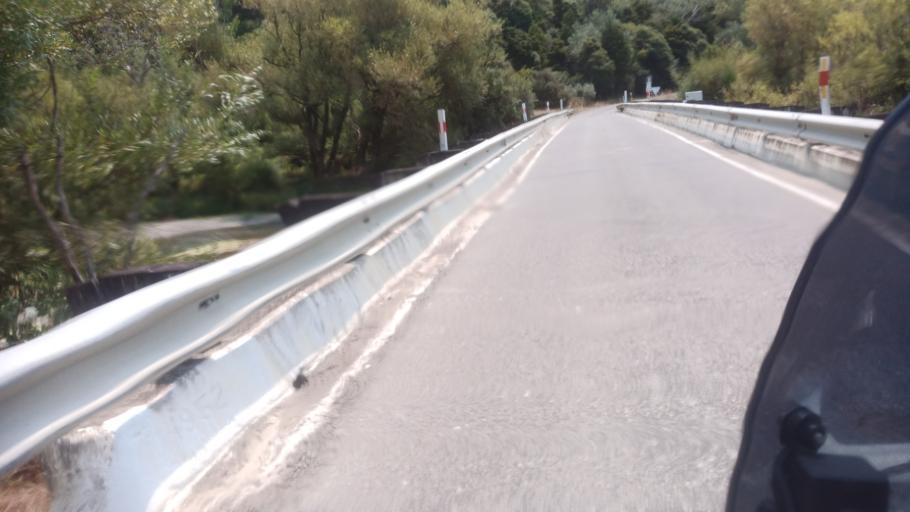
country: NZ
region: Bay of Plenty
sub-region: Opotiki District
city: Opotiki
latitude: -37.5929
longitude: 178.1528
